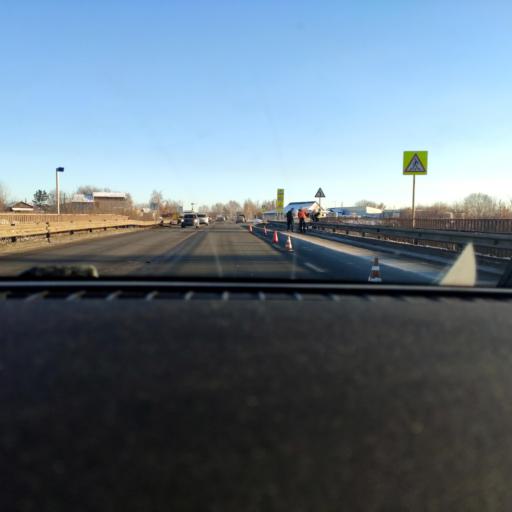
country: RU
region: Samara
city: Novokuybyshevsk
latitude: 53.0716
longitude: 50.0130
